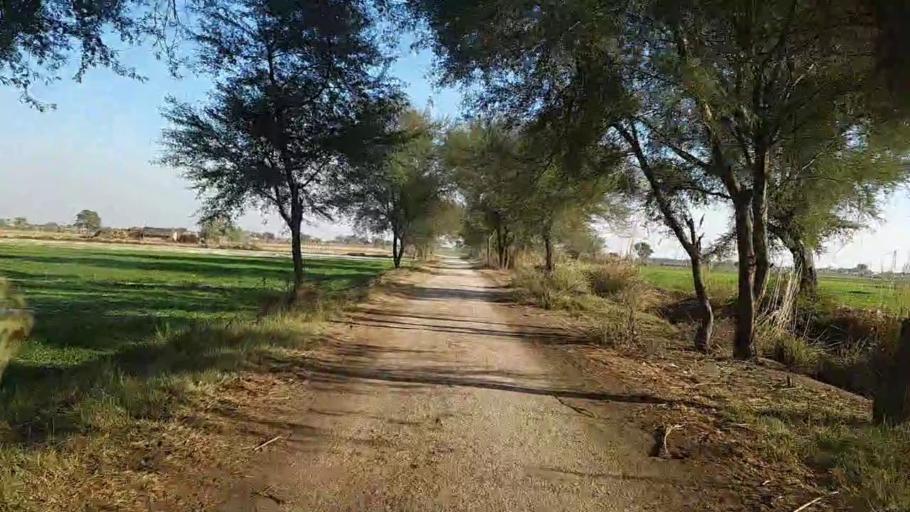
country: PK
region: Sindh
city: Khairpur
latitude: 27.9167
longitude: 69.7260
